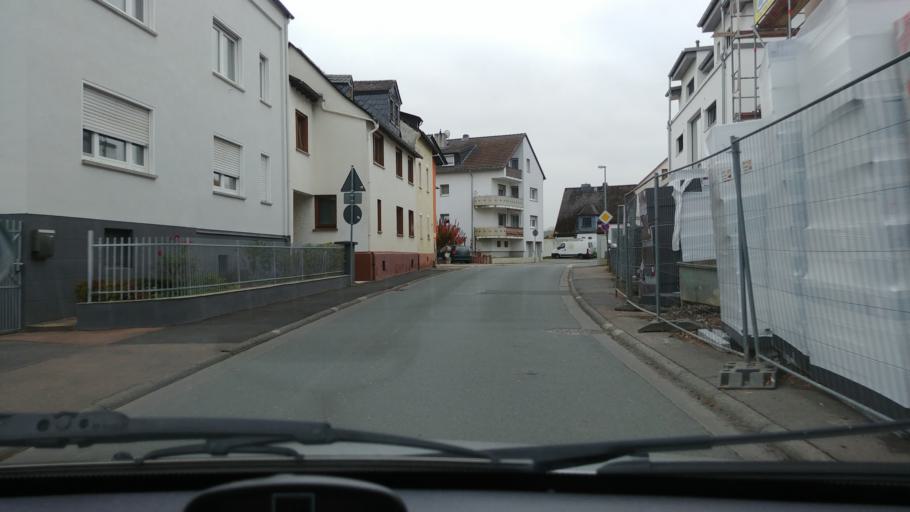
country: DE
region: Hesse
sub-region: Regierungsbezirk Giessen
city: Dehrn
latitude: 50.3967
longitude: 8.1022
